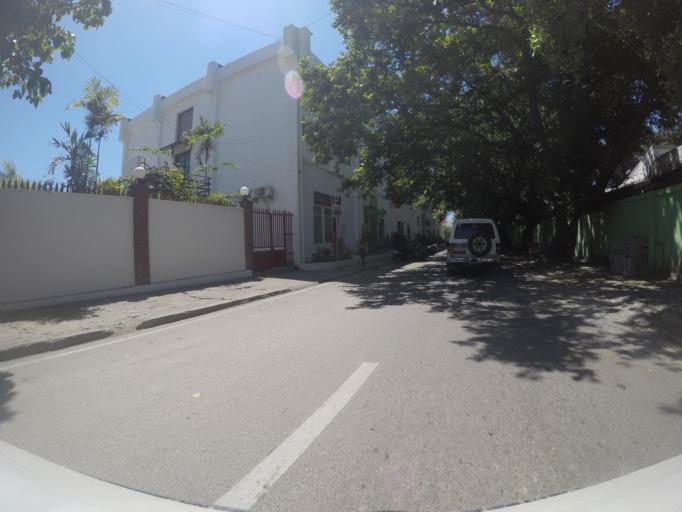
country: TL
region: Dili
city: Dili
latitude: -8.5550
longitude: 125.5738
